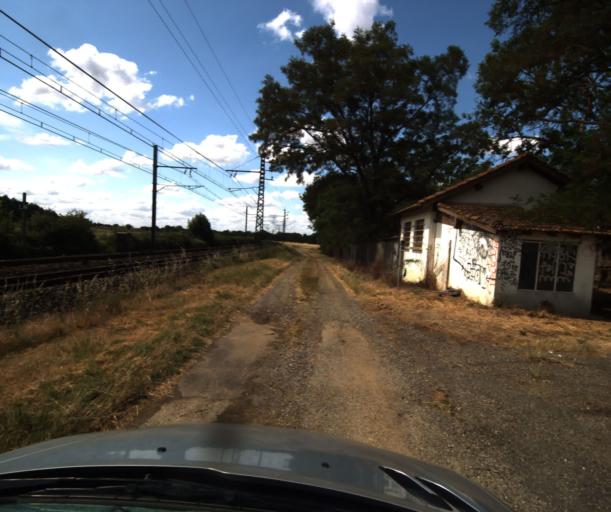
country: FR
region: Midi-Pyrenees
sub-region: Departement du Tarn-et-Garonne
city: Finhan
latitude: 43.9195
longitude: 1.2618
